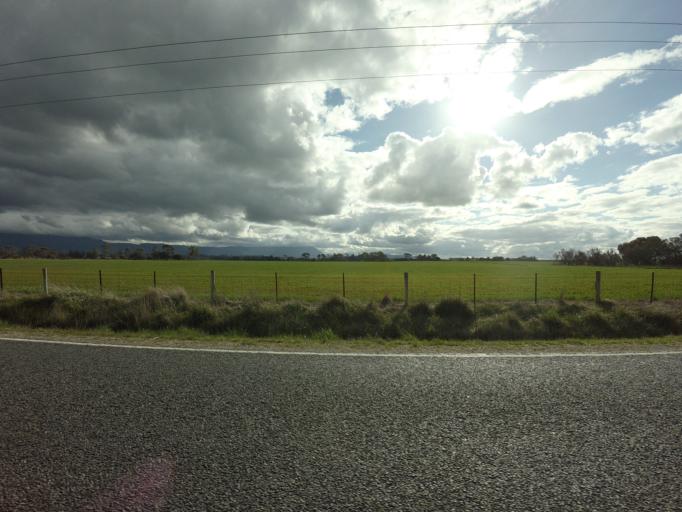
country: AU
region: Tasmania
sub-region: Northern Midlands
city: Longford
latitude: -41.7306
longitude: 147.0866
